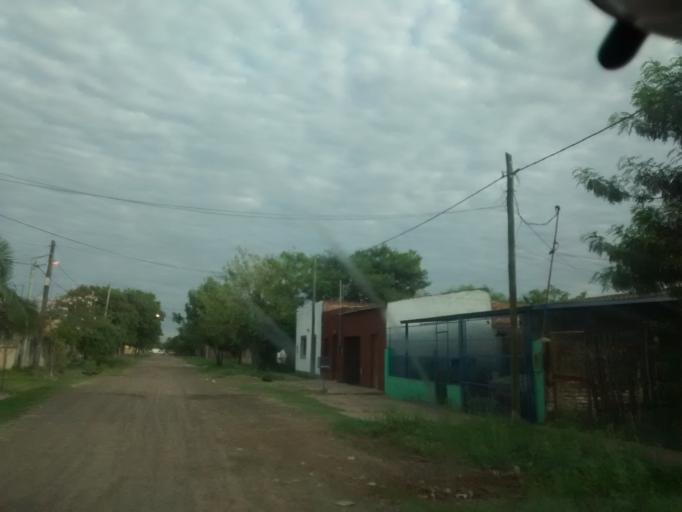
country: AR
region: Chaco
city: Resistencia
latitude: -27.4536
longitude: -59.0057
